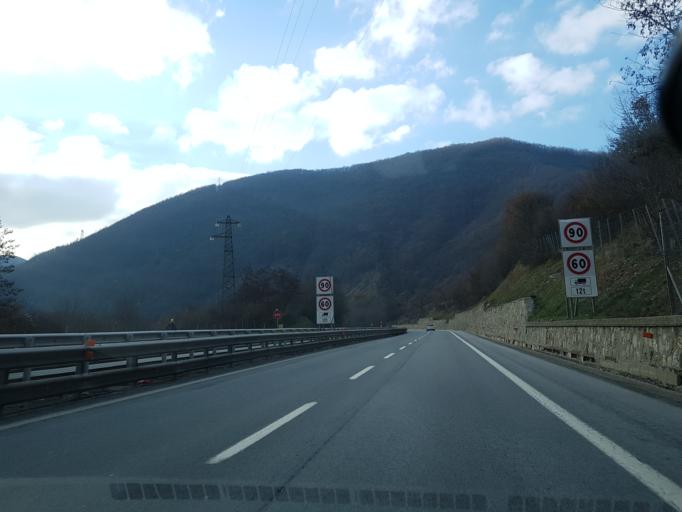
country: IT
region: Liguria
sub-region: Provincia di Genova
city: Isola del Cantone
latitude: 44.6659
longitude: 8.9344
